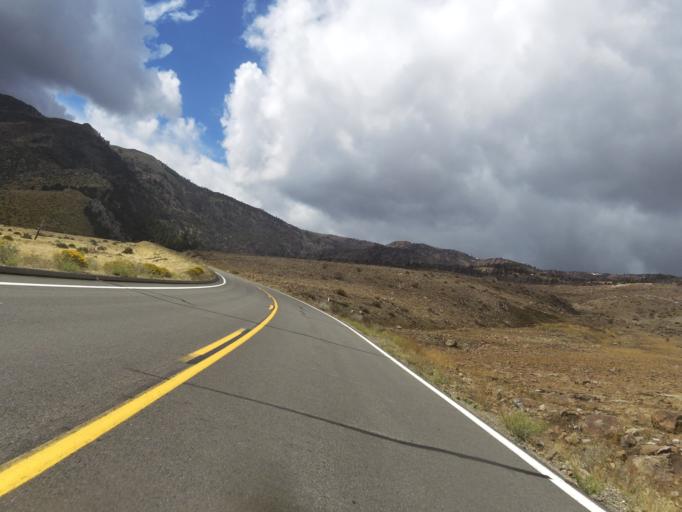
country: US
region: Nevada
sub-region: Lyon County
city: Smith Valley
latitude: 38.6551
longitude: -119.5802
